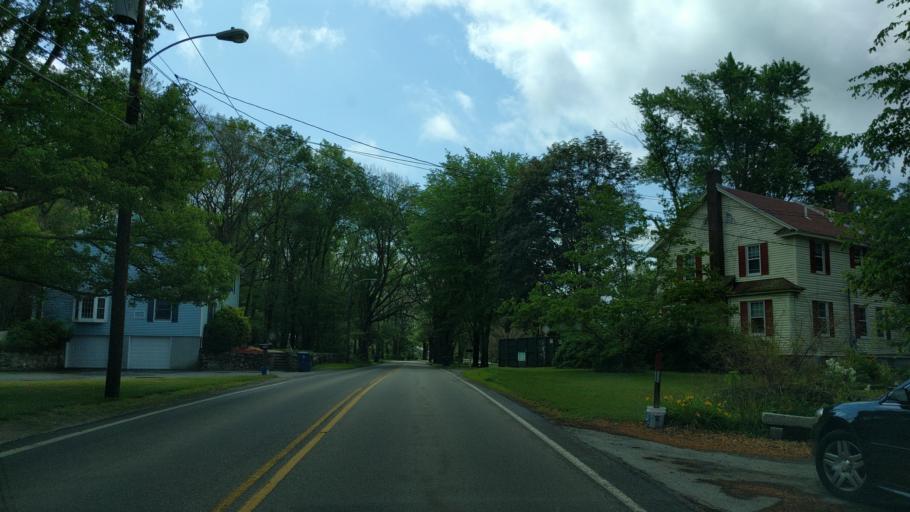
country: US
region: Massachusetts
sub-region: Worcester County
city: Whitinsville
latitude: 42.1246
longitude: -71.6970
